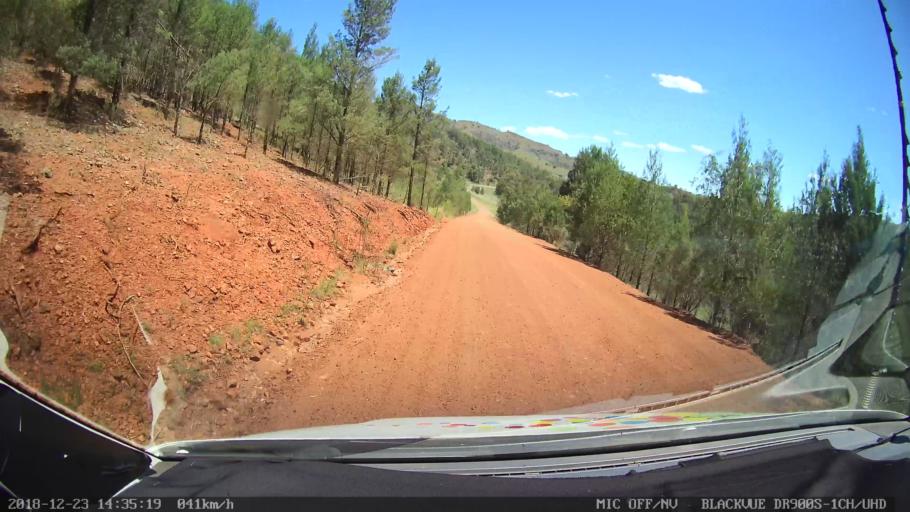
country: AU
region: New South Wales
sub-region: Tamworth Municipality
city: Manilla
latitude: -30.6094
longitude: 150.9077
